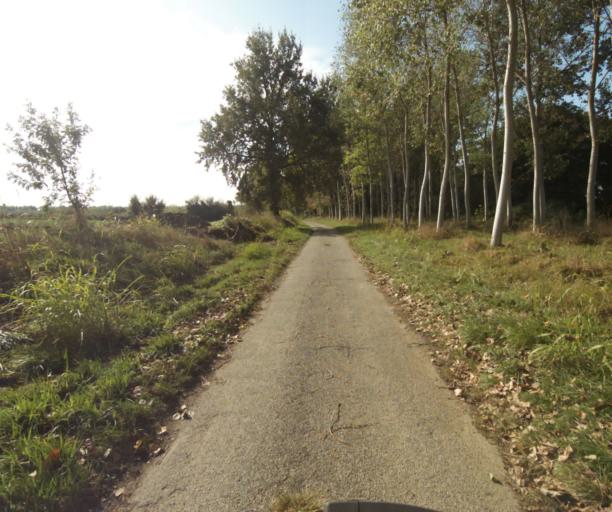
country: FR
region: Midi-Pyrenees
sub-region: Departement du Tarn-et-Garonne
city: Finhan
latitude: 43.8966
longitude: 1.2108
